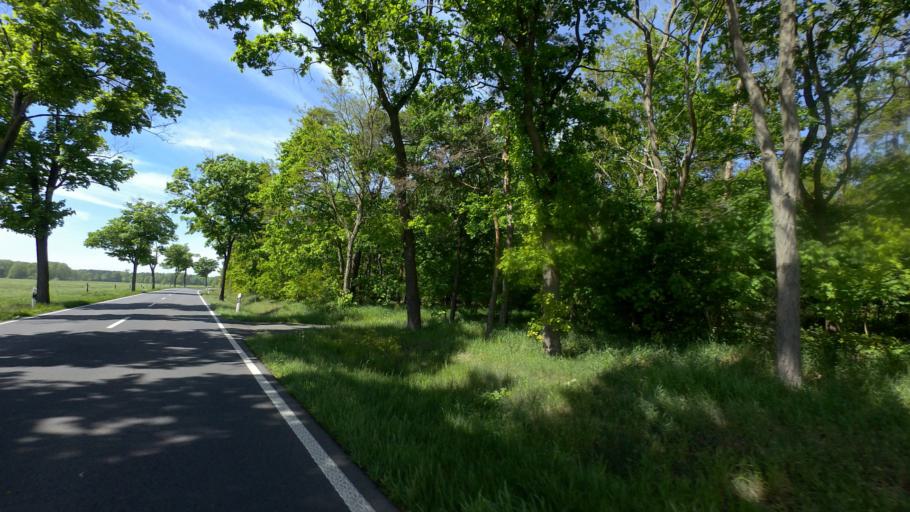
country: DE
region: Brandenburg
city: Baruth
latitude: 52.0628
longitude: 13.4937
